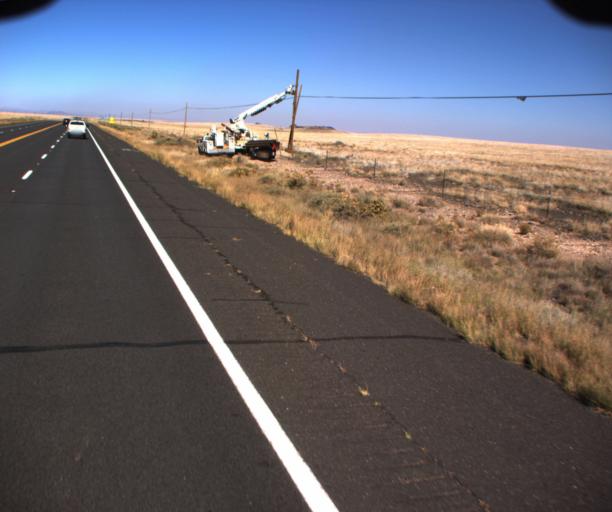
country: US
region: Arizona
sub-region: Coconino County
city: Flagstaff
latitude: 35.6293
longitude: -111.5202
